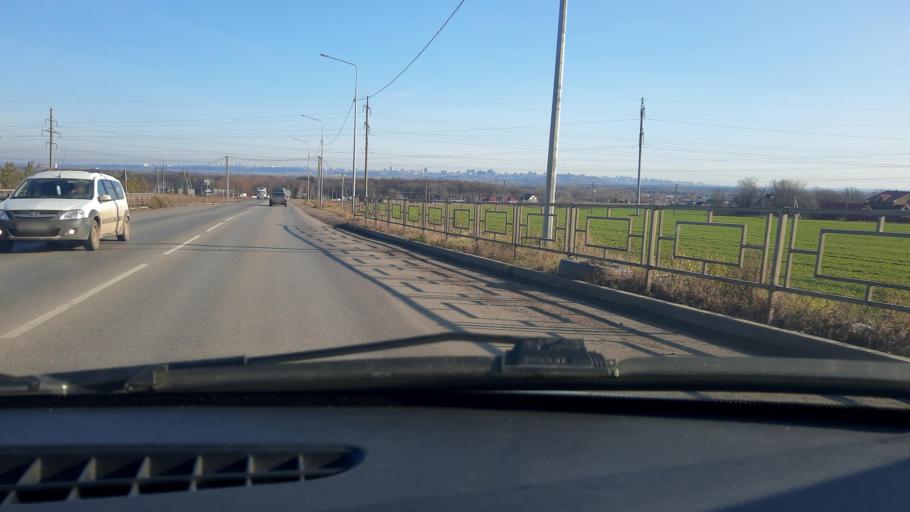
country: RU
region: Bashkortostan
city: Avdon
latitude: 54.7416
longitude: 55.7901
